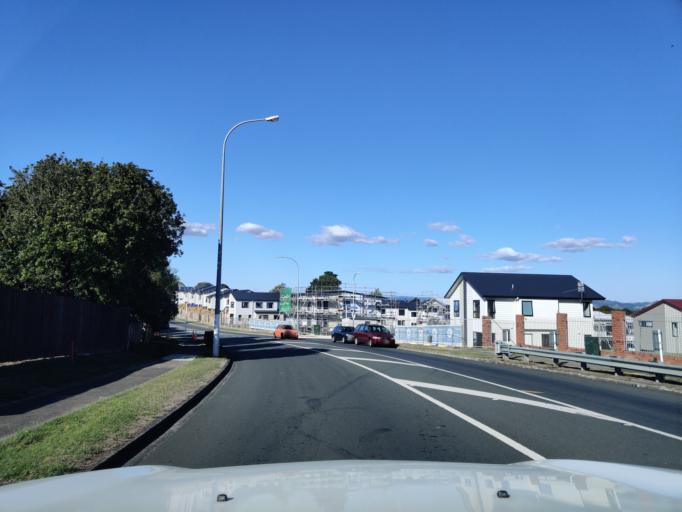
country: NZ
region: Auckland
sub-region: Auckland
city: Takanini
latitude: -37.0397
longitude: 174.8841
